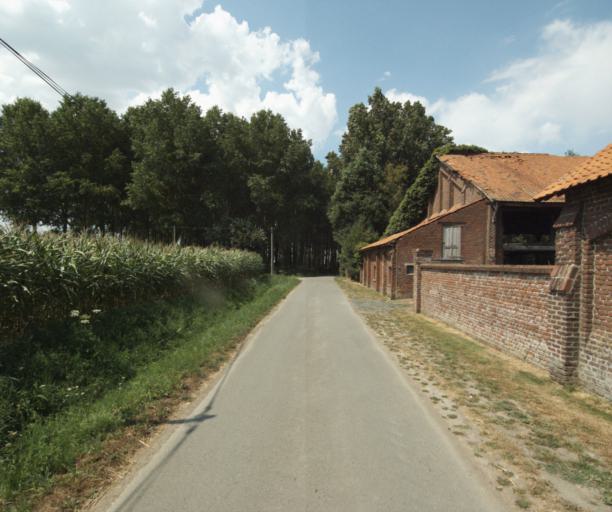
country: FR
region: Nord-Pas-de-Calais
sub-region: Departement du Nord
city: Comines
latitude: 50.7486
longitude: 2.9972
